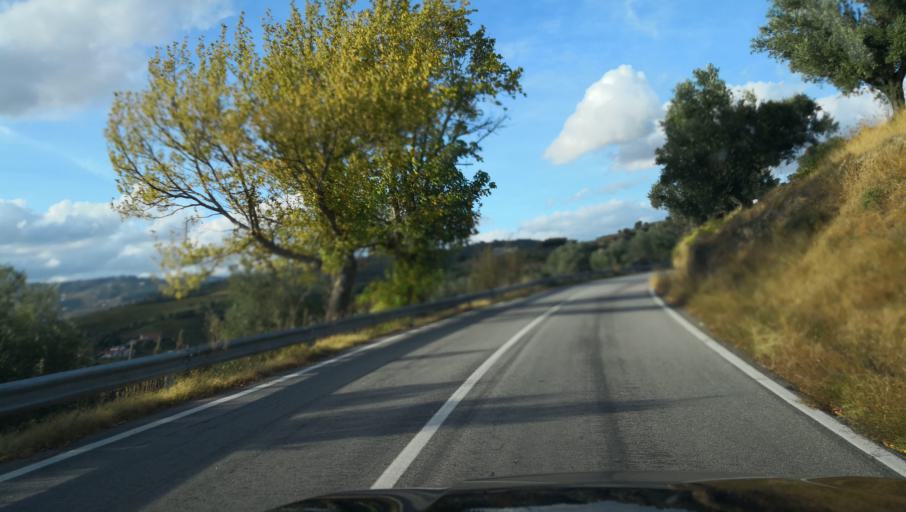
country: PT
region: Vila Real
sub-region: Peso da Regua
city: Peso da Regua
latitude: 41.1713
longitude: -7.7773
